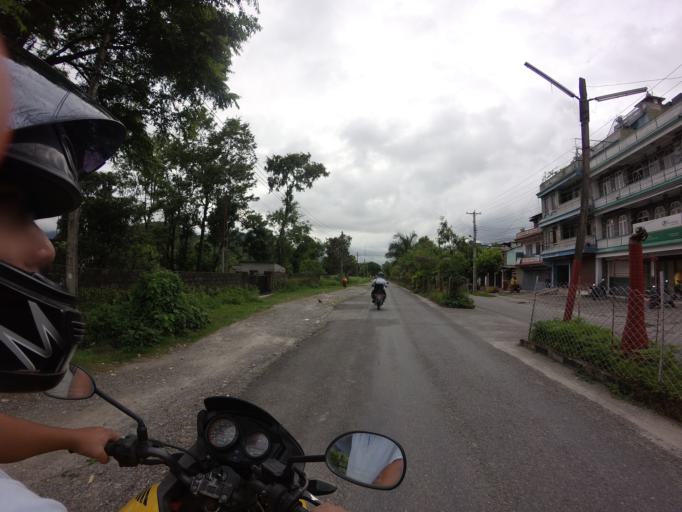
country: NP
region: Western Region
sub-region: Gandaki Zone
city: Pokhara
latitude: 28.1993
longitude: 83.9740
